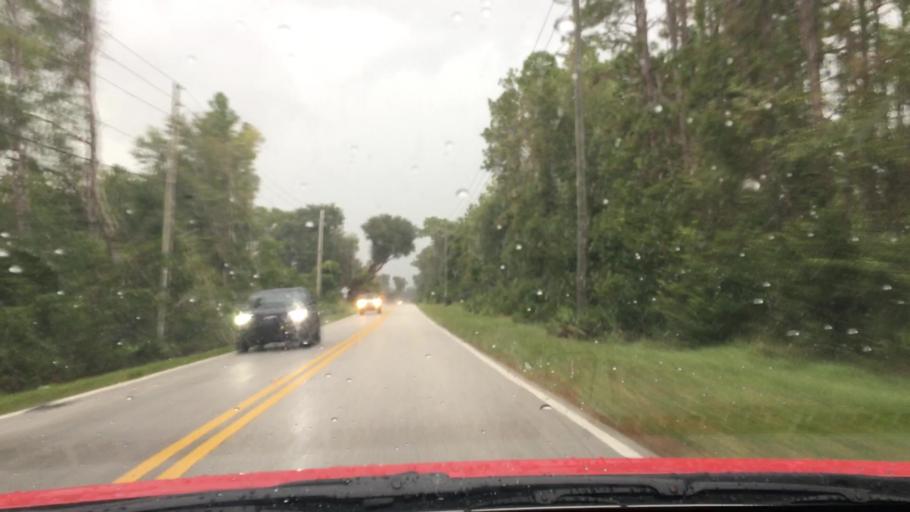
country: US
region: Florida
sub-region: Pasco County
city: Land O' Lakes
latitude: 28.2579
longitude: -82.4497
